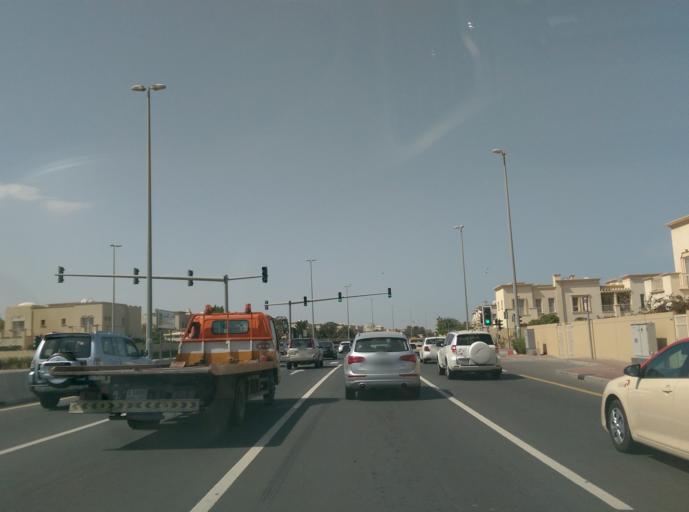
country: AE
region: Dubai
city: Dubai
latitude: 25.0619
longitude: 55.1862
